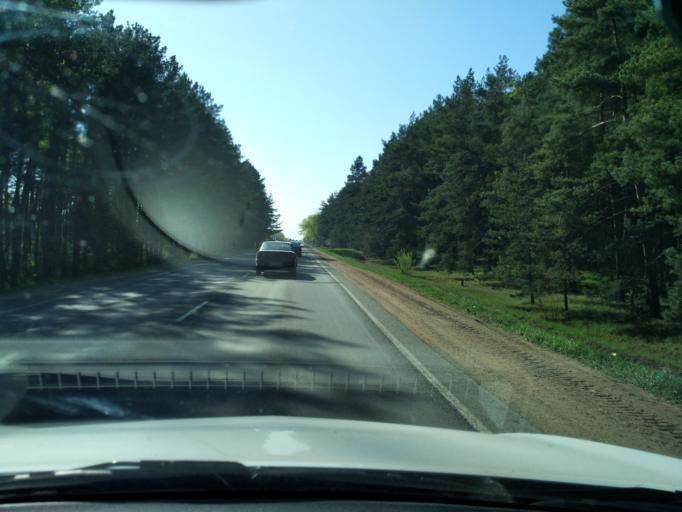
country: BY
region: Minsk
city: Borovlyany
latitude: 53.9659
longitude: 27.6551
